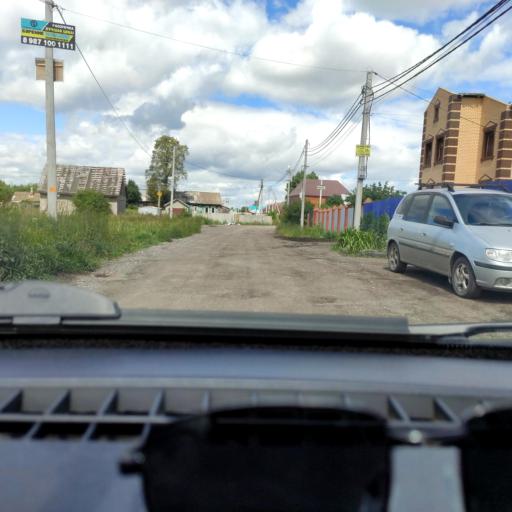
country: RU
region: Bashkortostan
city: Ufa
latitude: 54.6740
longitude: 56.0932
